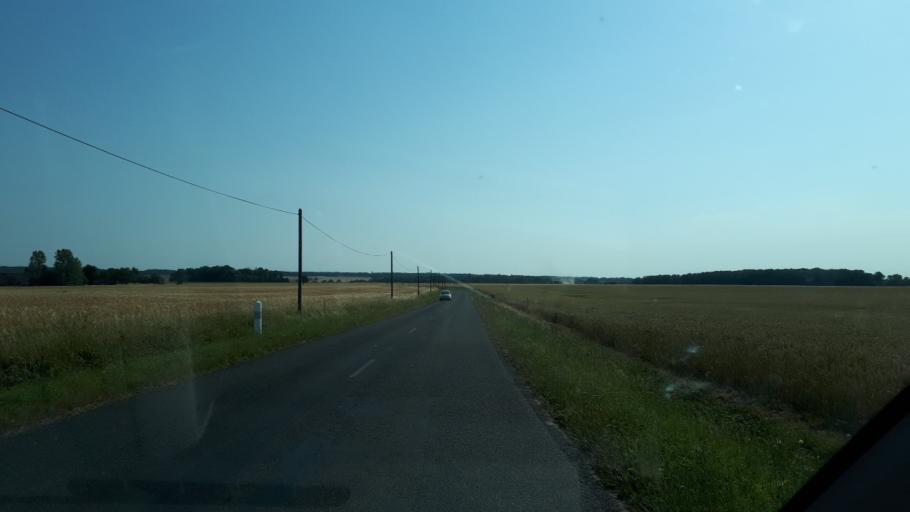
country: FR
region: Centre
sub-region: Departement du Loir-et-Cher
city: Droue
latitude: 48.0504
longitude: 1.0996
